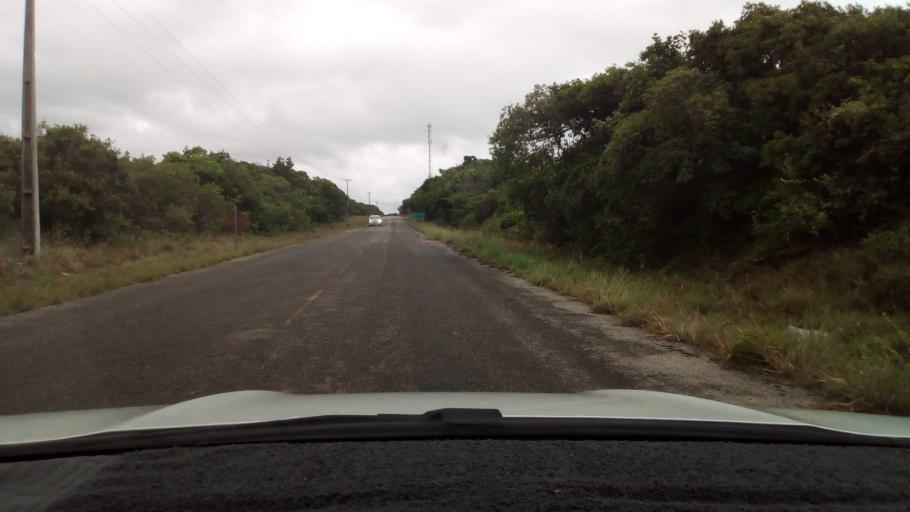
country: BR
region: Paraiba
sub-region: Pitimbu
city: Pitimbu
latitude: -7.3532
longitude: -34.8034
